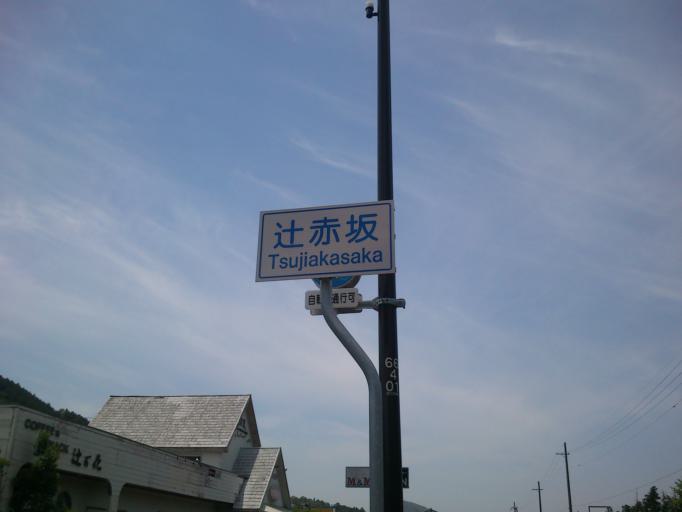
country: JP
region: Kyoto
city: Ayabe
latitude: 35.2090
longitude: 135.2460
